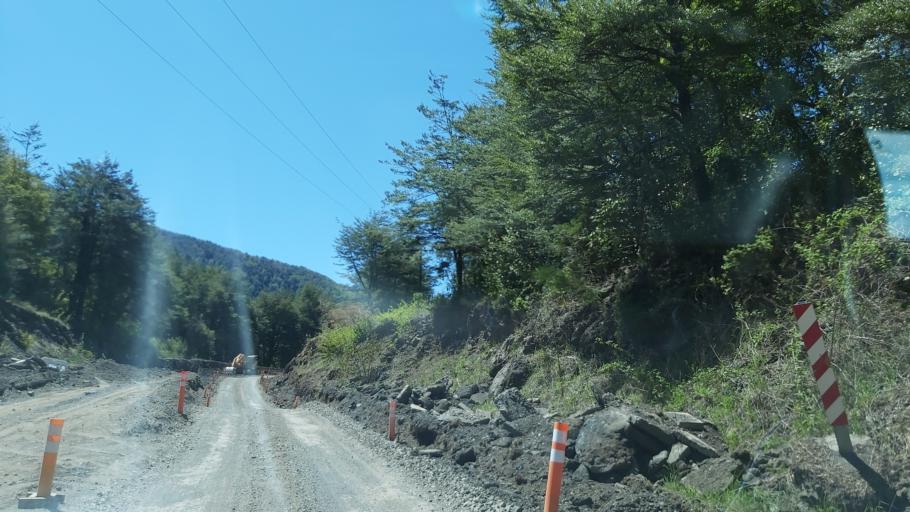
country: CL
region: Araucania
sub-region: Provincia de Cautin
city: Vilcun
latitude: -38.4715
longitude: -71.6766
